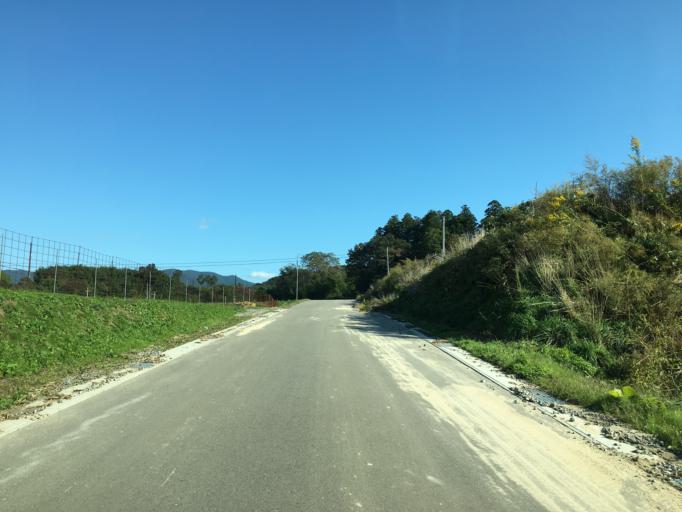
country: JP
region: Fukushima
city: Fukushima-shi
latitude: 37.6674
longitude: 140.5723
